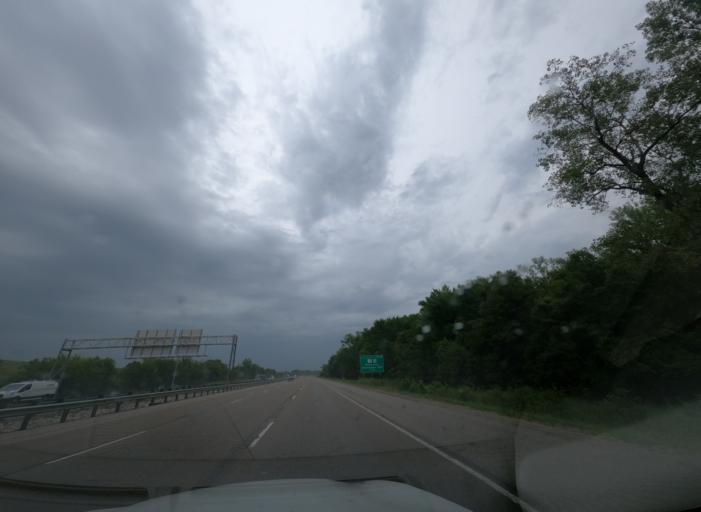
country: US
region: Illinois
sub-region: Saint Clair County
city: Fairmont City
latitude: 38.6545
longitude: -90.1148
